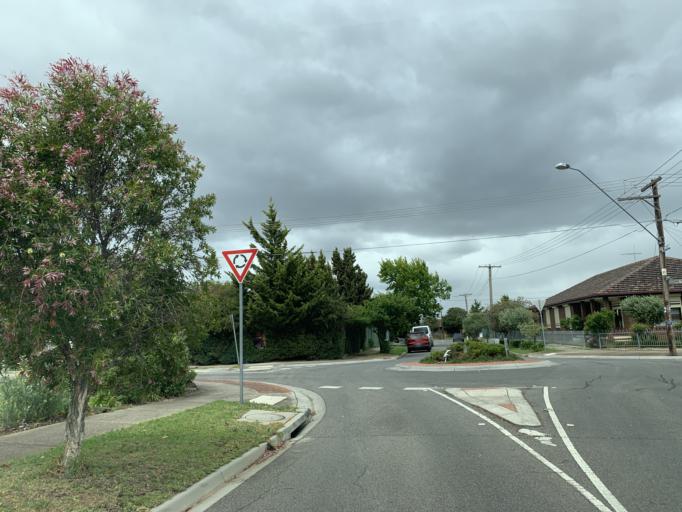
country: AU
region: Victoria
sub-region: Brimbank
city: Kealba
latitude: -37.7459
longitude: 144.8239
